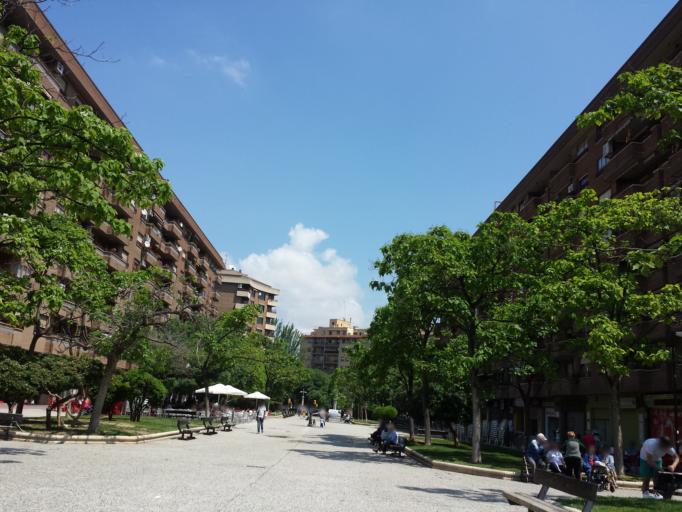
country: ES
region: Aragon
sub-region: Provincia de Zaragoza
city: Almozara
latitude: 41.6587
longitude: -0.8958
